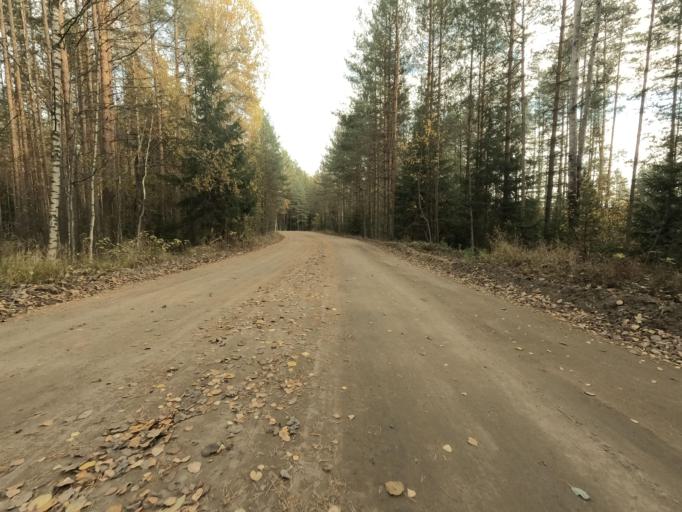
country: RU
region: Leningrad
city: Priladozhskiy
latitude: 59.6353
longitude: 31.3933
